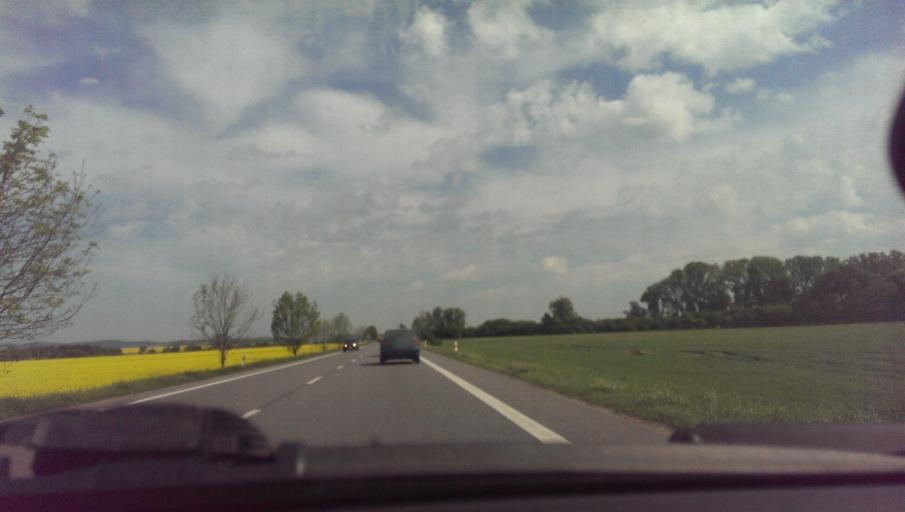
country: CZ
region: Zlin
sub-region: Okres Uherske Hradiste
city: Uherske Hradiste
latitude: 49.0967
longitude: 17.4537
